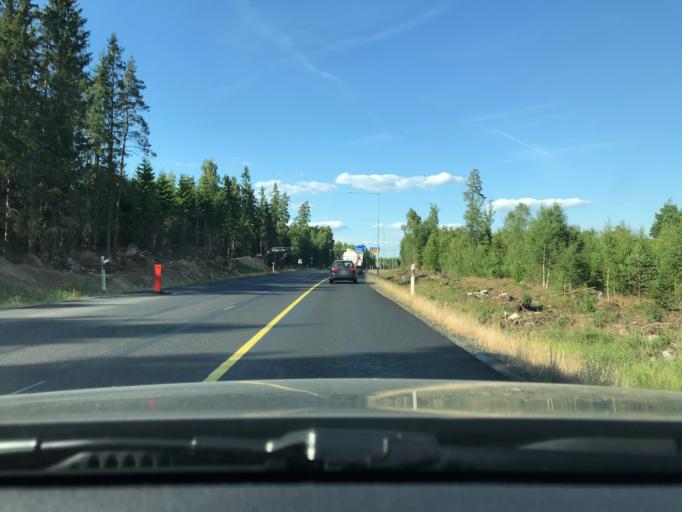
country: SE
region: Kronoberg
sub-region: Almhults Kommun
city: AElmhult
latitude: 56.5858
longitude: 14.1917
